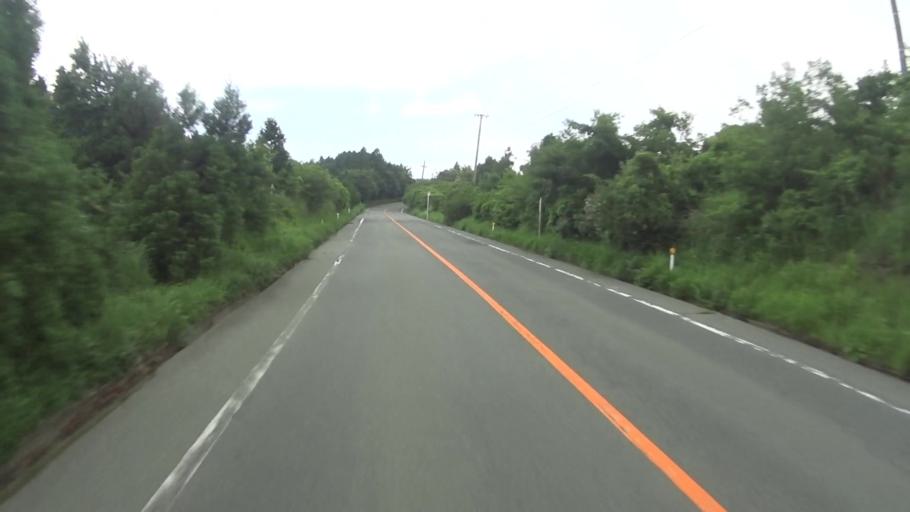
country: JP
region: Kumamoto
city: Aso
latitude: 32.9619
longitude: 130.9961
